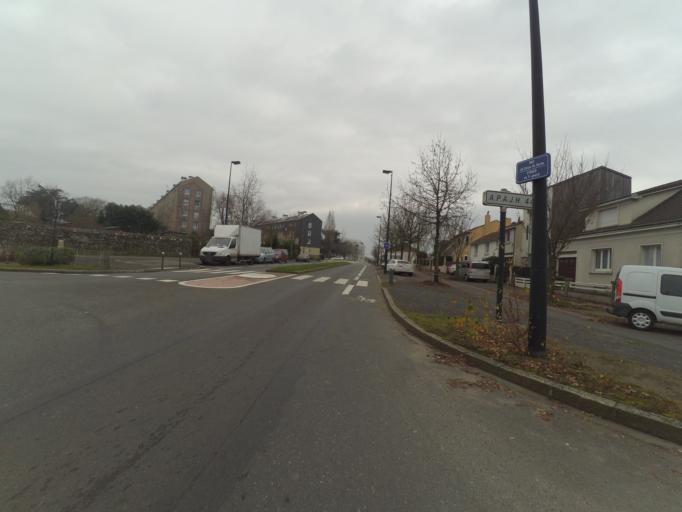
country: FR
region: Pays de la Loire
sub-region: Departement de la Loire-Atlantique
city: Bouguenais
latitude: 47.2175
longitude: -1.6019
